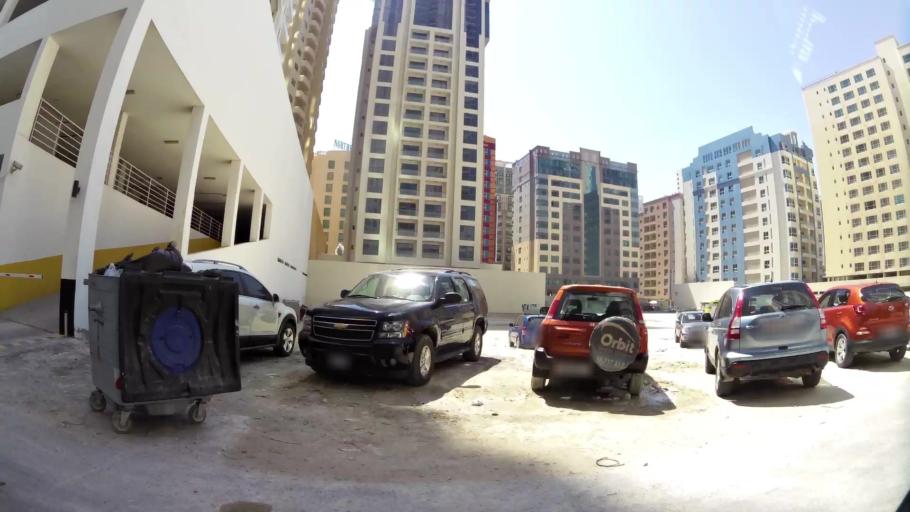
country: BH
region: Manama
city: Manama
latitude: 26.2230
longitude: 50.6094
